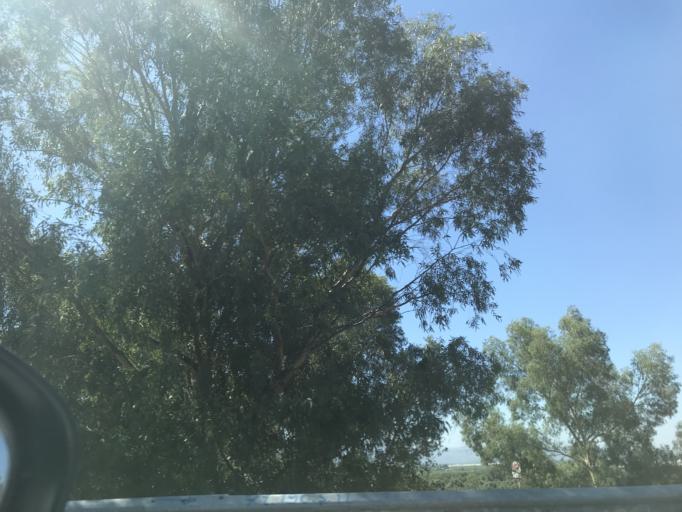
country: TR
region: Aydin
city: Germencik
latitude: 37.8692
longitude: 27.6530
